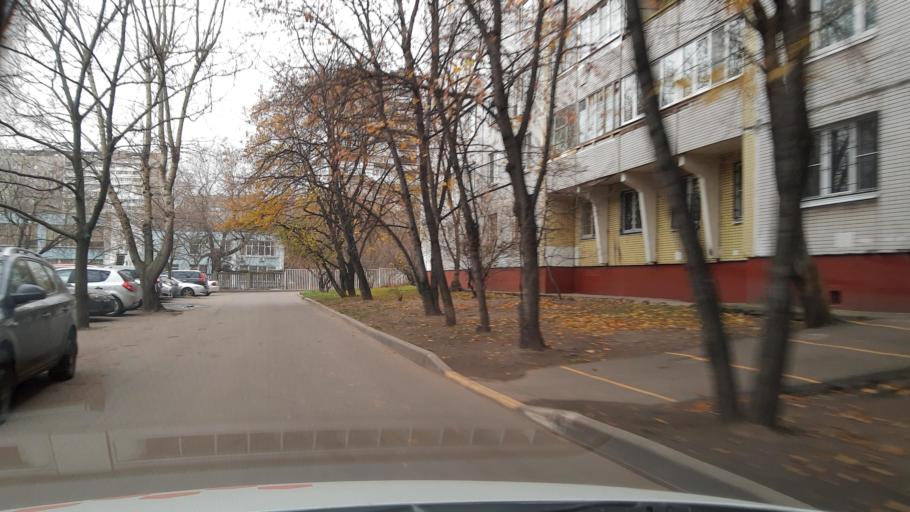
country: RU
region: Moscow
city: Lyublino
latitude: 55.6780
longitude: 37.7709
